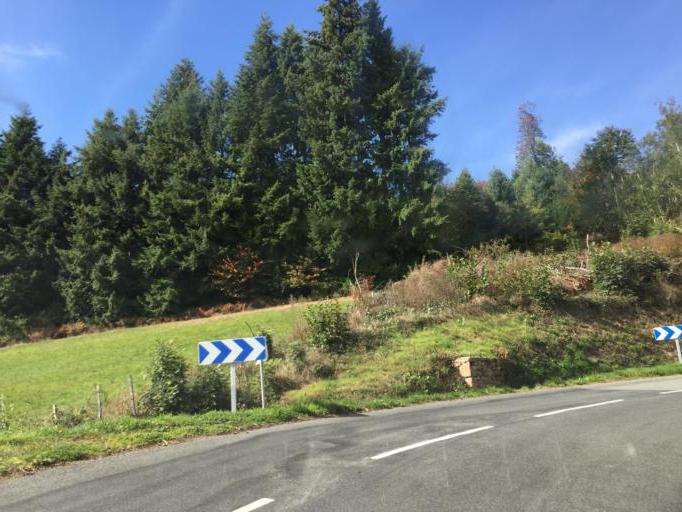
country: FR
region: Rhone-Alpes
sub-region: Departement du Rhone
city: Grandris
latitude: 46.0848
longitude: 4.4601
